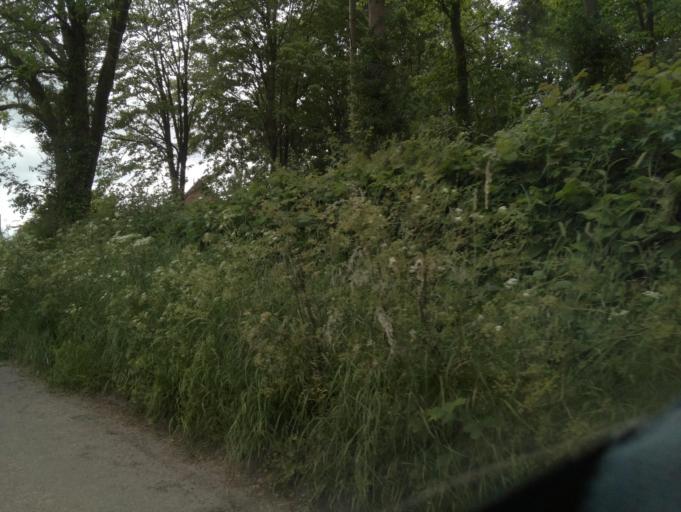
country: GB
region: England
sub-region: Herefordshire
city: Ledbury
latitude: 52.0307
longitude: -2.4751
